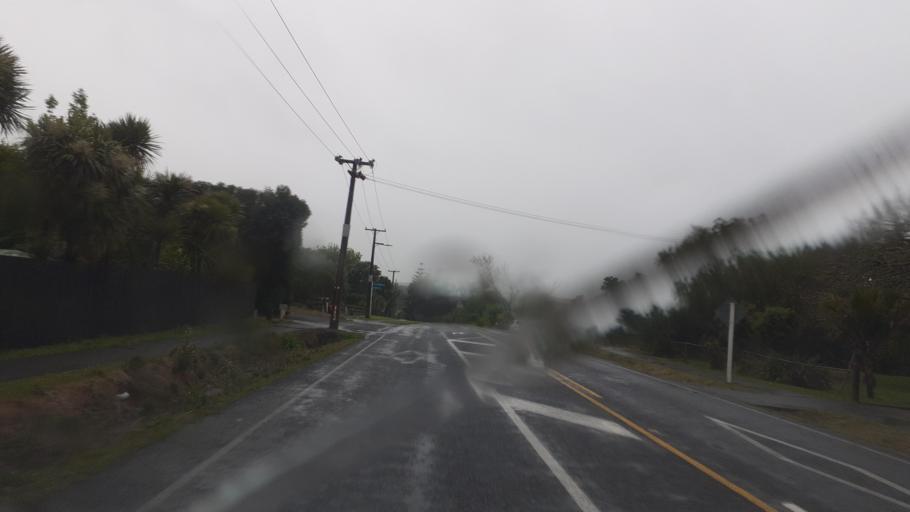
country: NZ
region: Northland
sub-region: Far North District
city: Kerikeri
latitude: -35.2071
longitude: 173.9651
